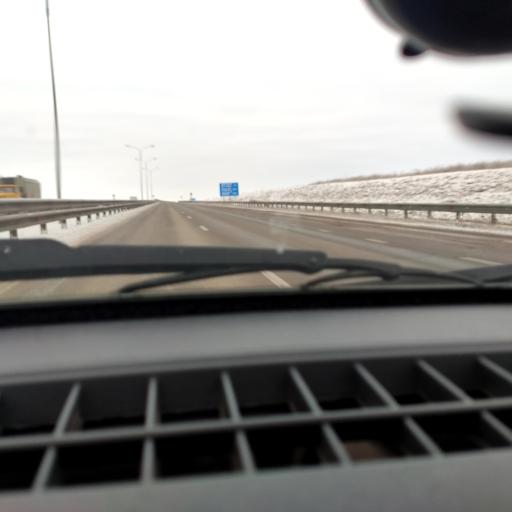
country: RU
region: Bashkortostan
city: Kushnarenkovo
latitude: 55.0812
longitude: 55.2681
